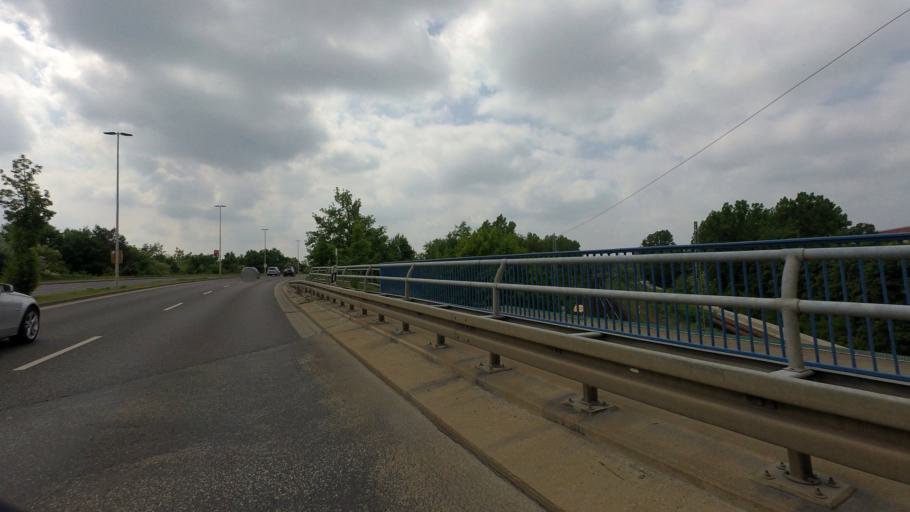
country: DE
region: Brandenburg
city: Cottbus
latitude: 51.7577
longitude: 14.3586
